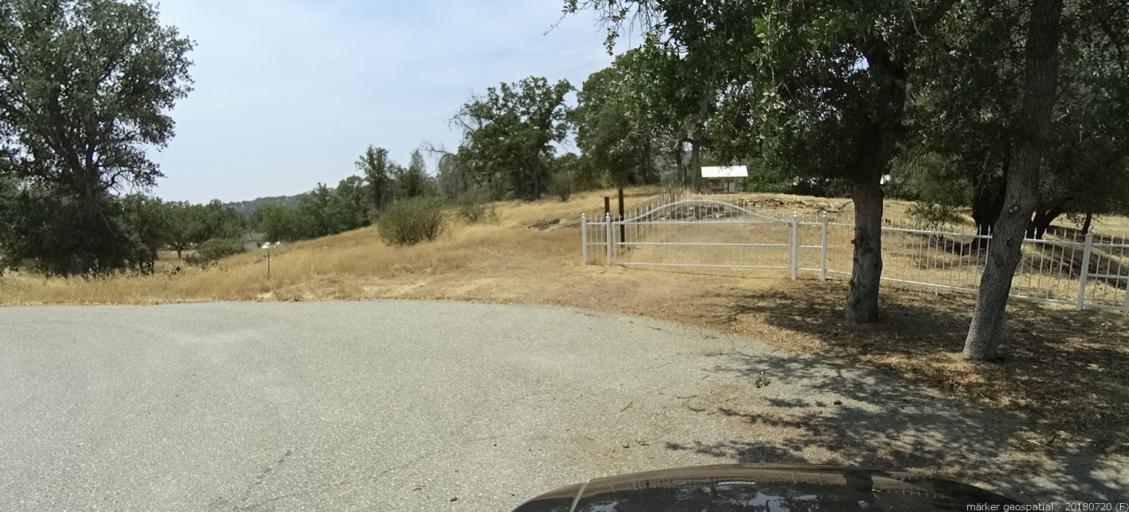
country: US
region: California
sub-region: Madera County
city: Yosemite Lakes
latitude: 37.2367
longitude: -119.7706
